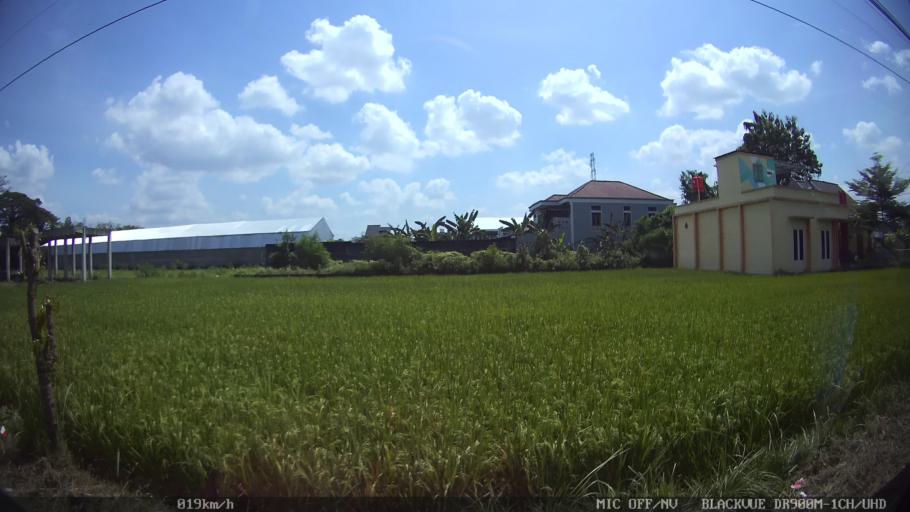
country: ID
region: Daerah Istimewa Yogyakarta
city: Sewon
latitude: -7.8477
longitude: 110.3887
